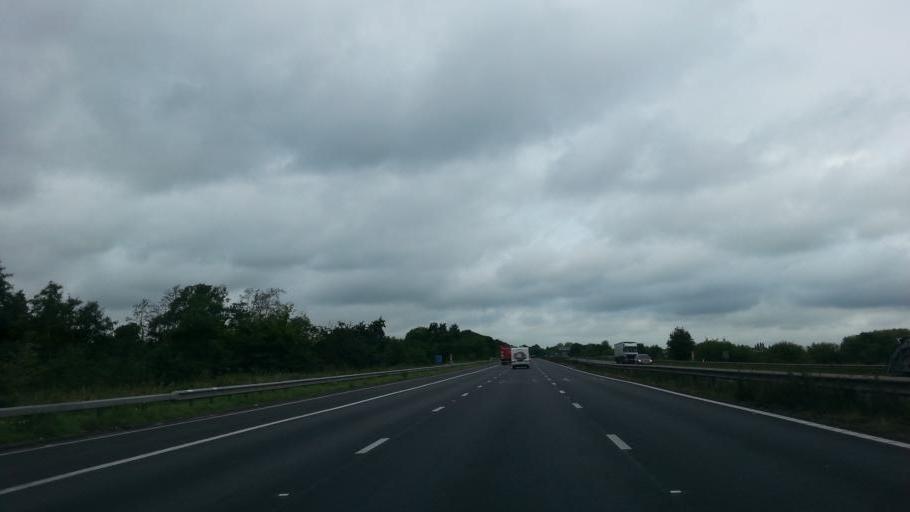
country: GB
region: England
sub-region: Leicestershire
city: Narborough
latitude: 52.5717
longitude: -1.1937
